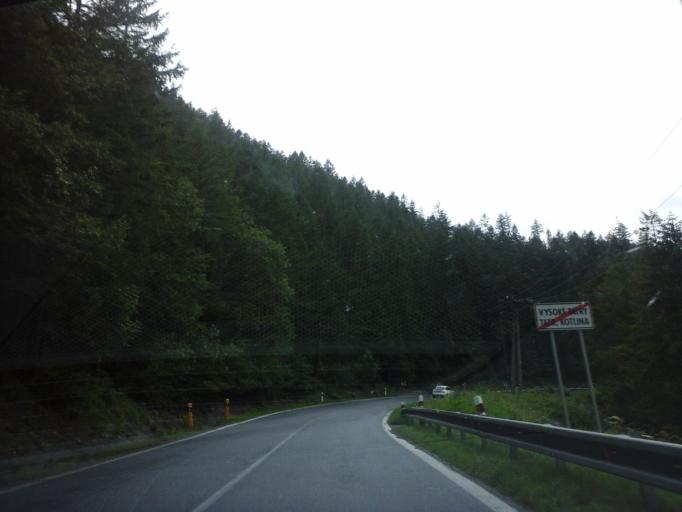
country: SK
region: Presovsky
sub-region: Okres Poprad
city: Zdiar
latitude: 49.2318
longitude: 20.3145
